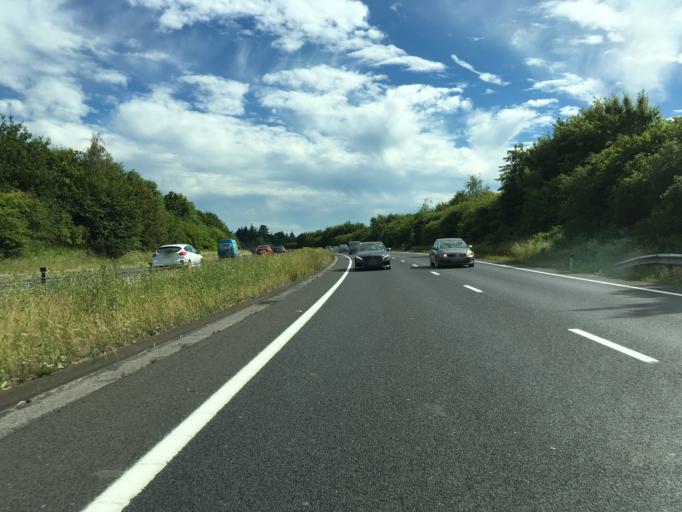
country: GB
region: England
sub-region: Hampshire
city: Highclere
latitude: 51.3720
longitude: -1.3645
